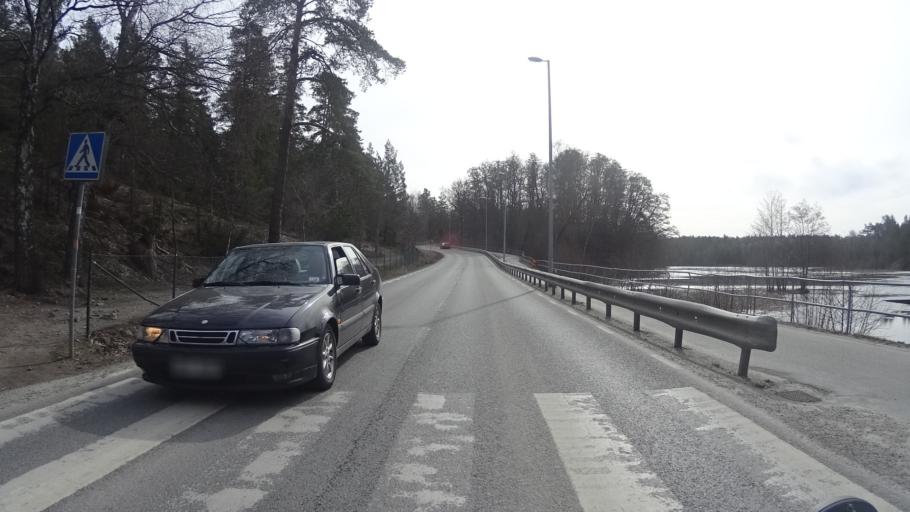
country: SE
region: Stockholm
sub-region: Nacka Kommun
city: Nacka
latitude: 59.2946
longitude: 18.1447
